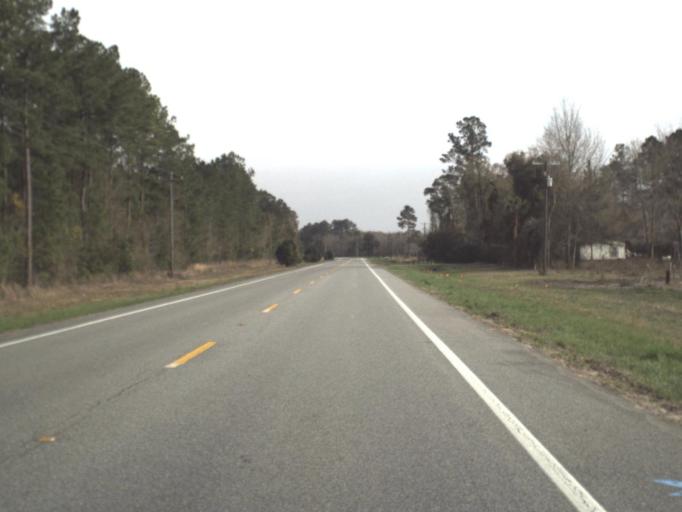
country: US
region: Florida
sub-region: Jefferson County
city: Monticello
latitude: 30.5116
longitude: -83.7758
